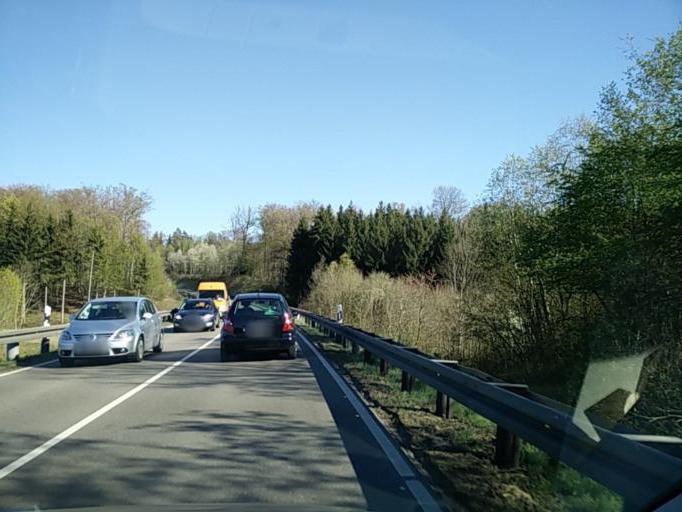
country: DE
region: Baden-Wuerttemberg
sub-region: Regierungsbezirk Stuttgart
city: Holzgerlingen
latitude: 48.6126
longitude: 9.0270
